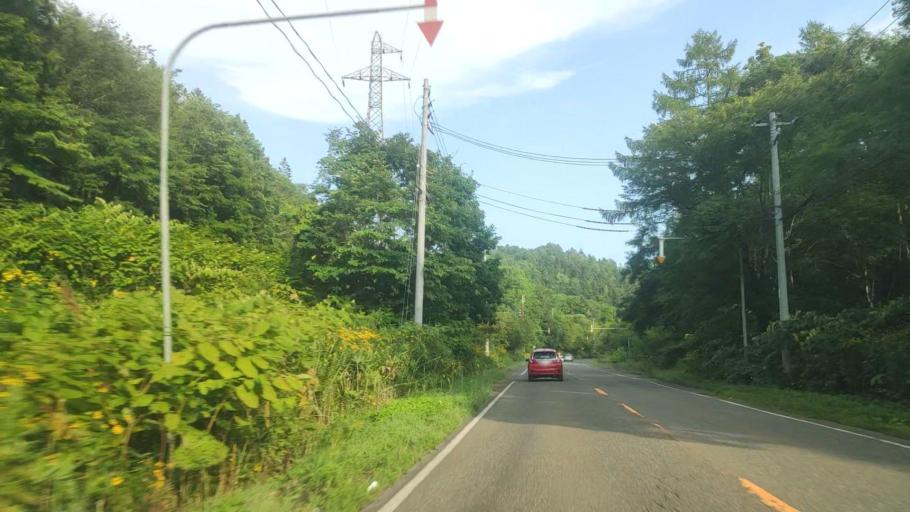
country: JP
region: Hokkaido
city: Iwamizawa
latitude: 43.0345
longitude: 141.9395
